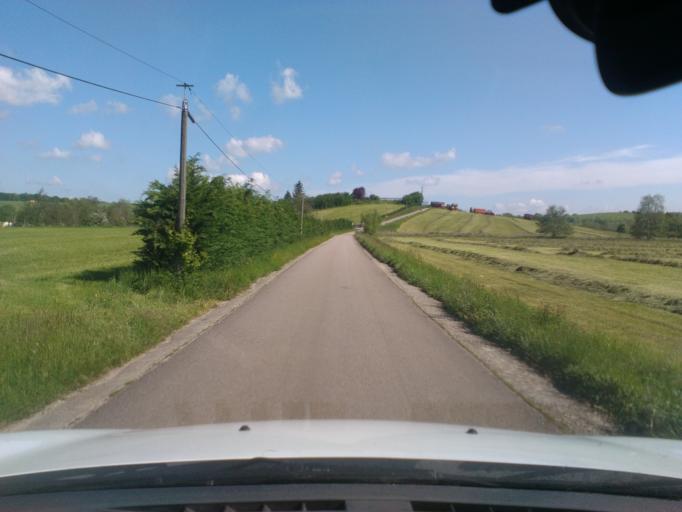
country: FR
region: Lorraine
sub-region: Departement des Vosges
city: Mirecourt
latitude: 48.3255
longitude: 6.1455
